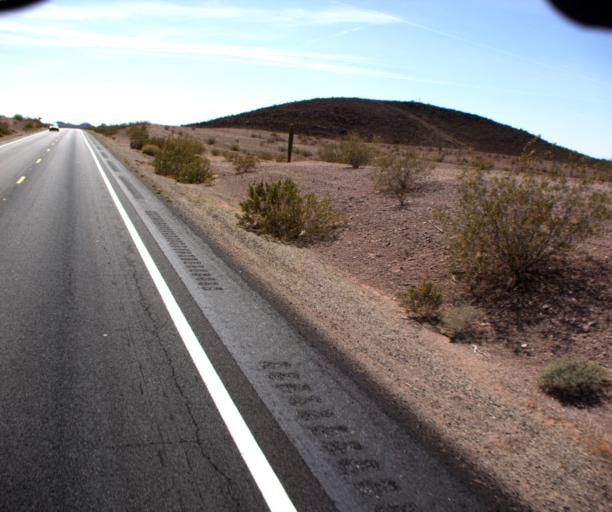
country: US
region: Arizona
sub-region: Yuma County
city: Wellton
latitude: 33.1072
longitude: -114.2964
